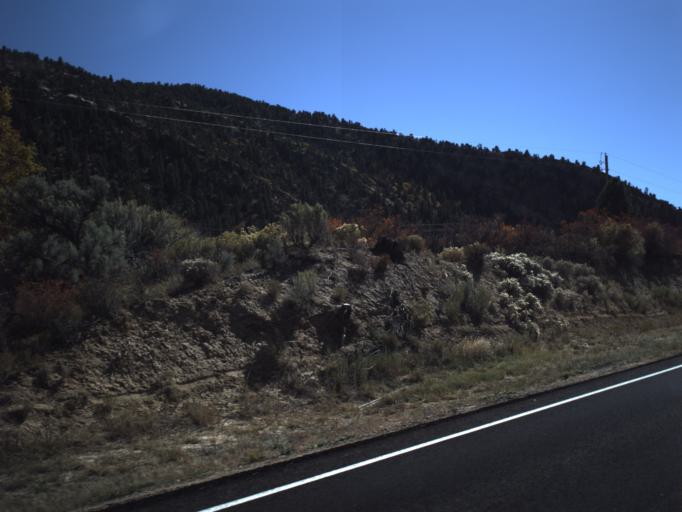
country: US
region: Utah
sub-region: Garfield County
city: Panguitch
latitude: 37.7208
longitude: -111.7808
